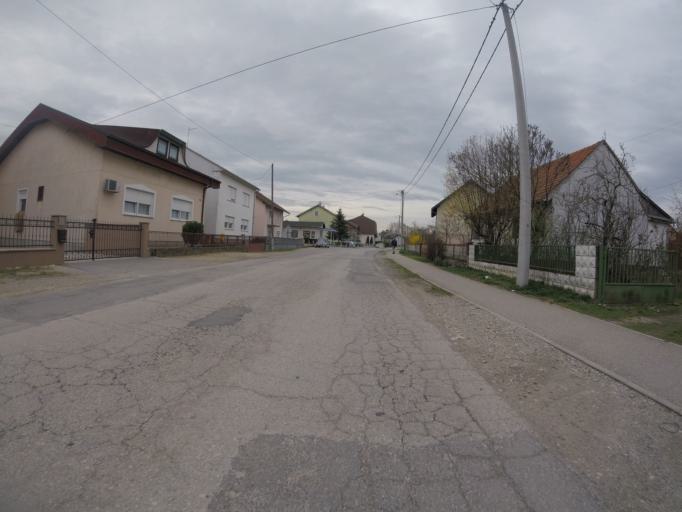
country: HR
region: Grad Zagreb
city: Odra
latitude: 45.7131
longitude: 16.0223
